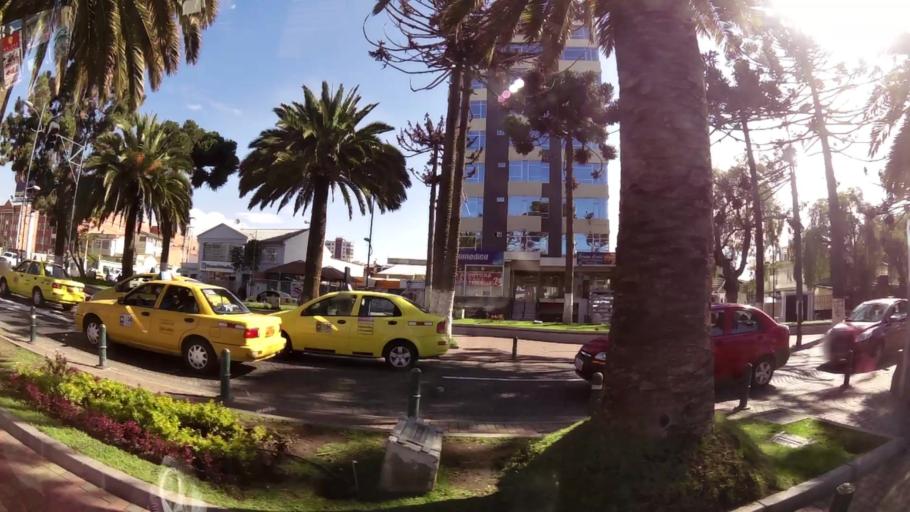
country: EC
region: Chimborazo
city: Riobamba
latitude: -1.6654
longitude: -78.6585
